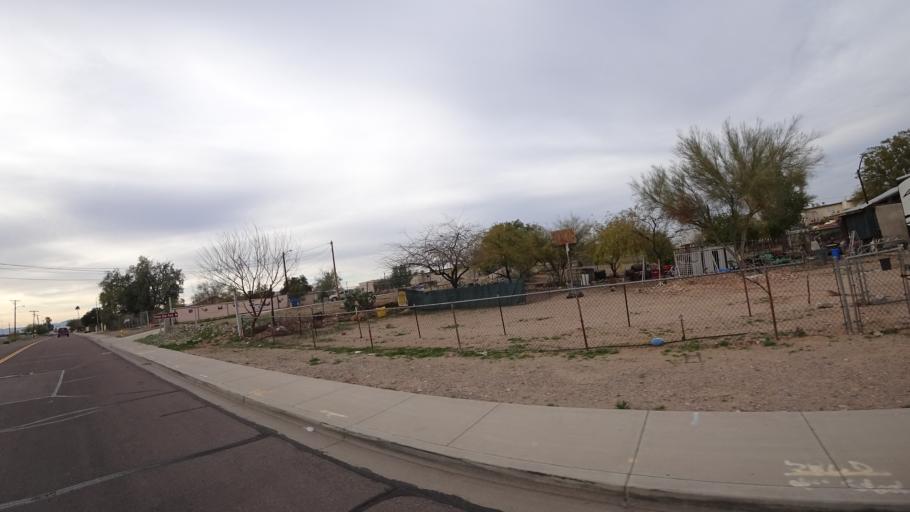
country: US
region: Arizona
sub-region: Maricopa County
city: El Mirage
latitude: 33.6235
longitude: -112.3253
